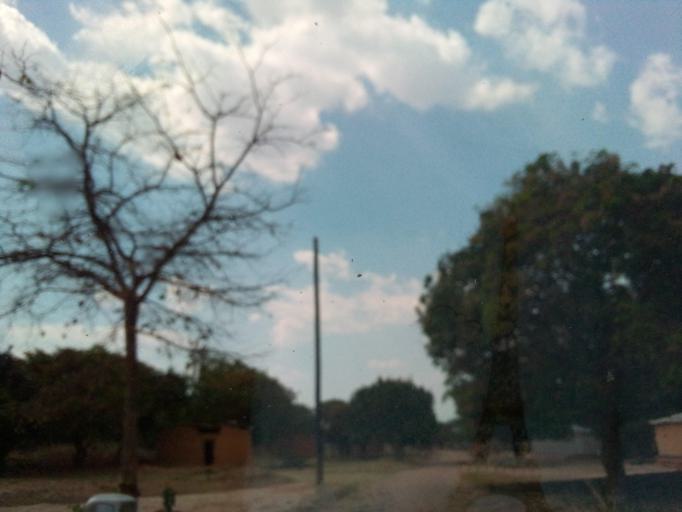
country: ZM
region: Northern
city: Mpika
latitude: -11.8354
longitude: 31.3876
